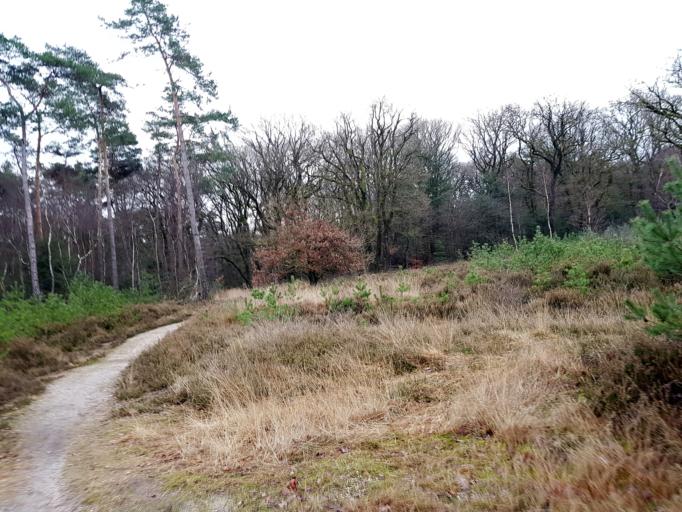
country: NL
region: Utrecht
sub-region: Gemeente Utrechtse Heuvelrug
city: Maarn
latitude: 52.0477
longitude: 5.3731
